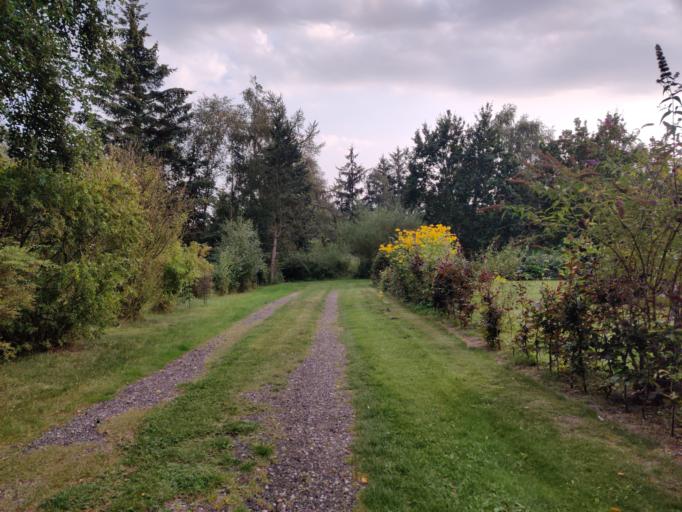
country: DK
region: Zealand
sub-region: Guldborgsund Kommune
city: Nykobing Falster
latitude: 54.6029
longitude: 11.9594
